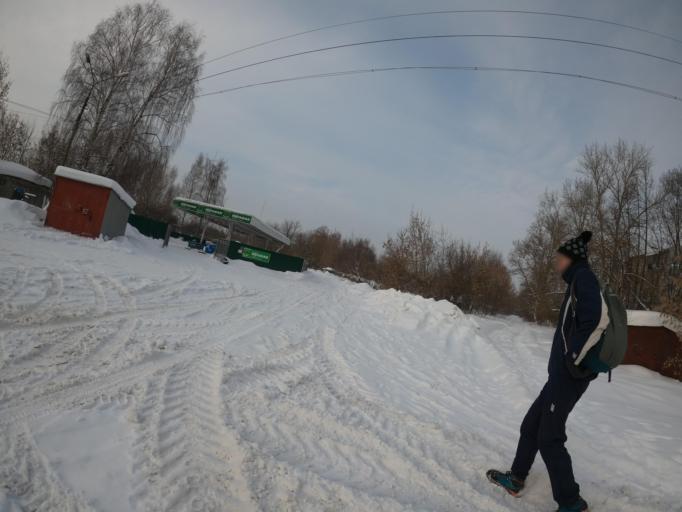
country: RU
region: Moskovskaya
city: Elektrogorsk
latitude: 55.8897
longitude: 38.7705
